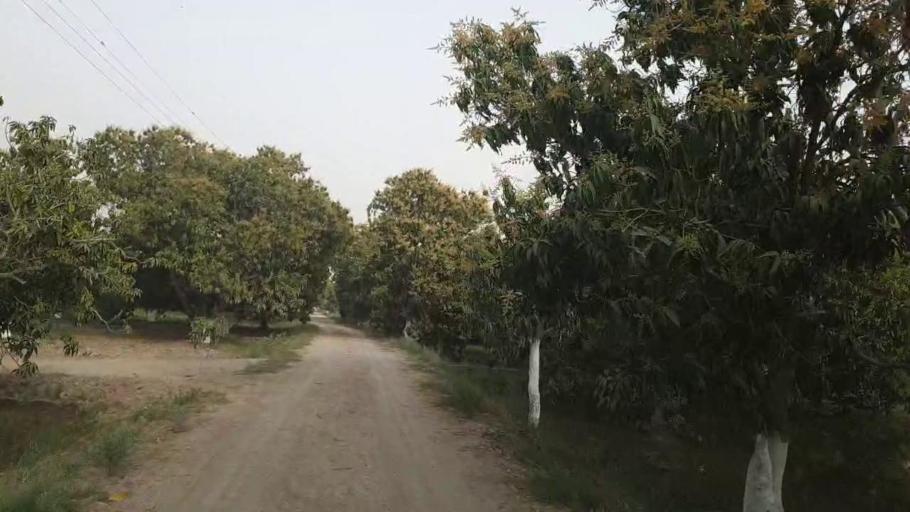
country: PK
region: Sindh
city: Kunri
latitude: 25.0677
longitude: 69.4392
